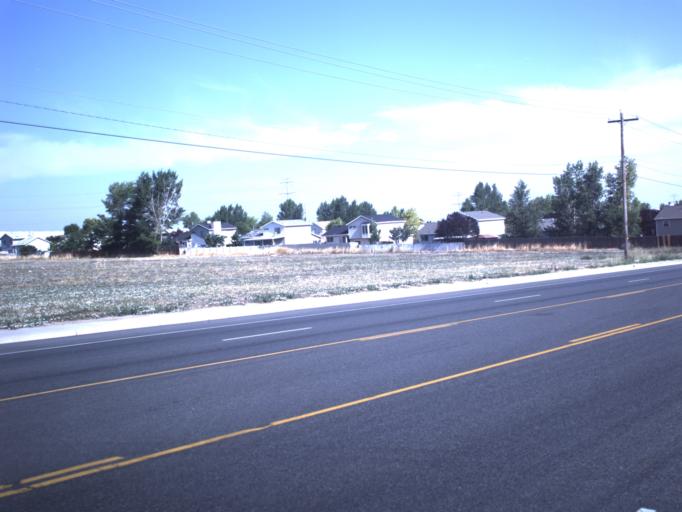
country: US
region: Utah
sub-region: Salt Lake County
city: Kearns
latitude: 40.6701
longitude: -112.0246
